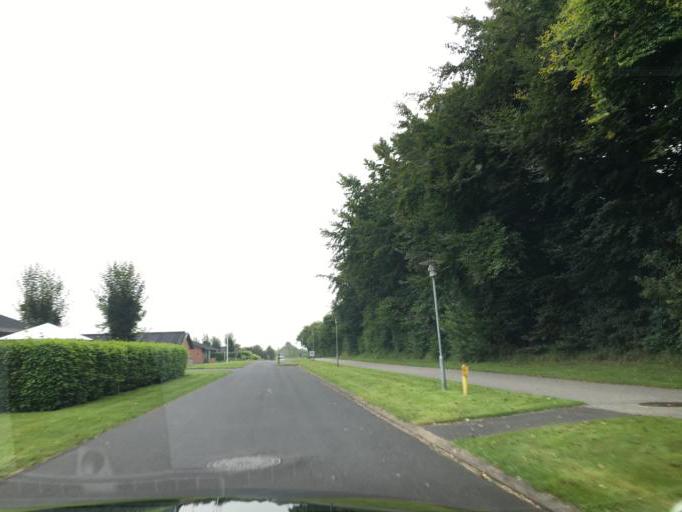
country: DK
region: South Denmark
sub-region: Kolding Kommune
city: Kolding
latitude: 55.5632
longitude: 9.4846
